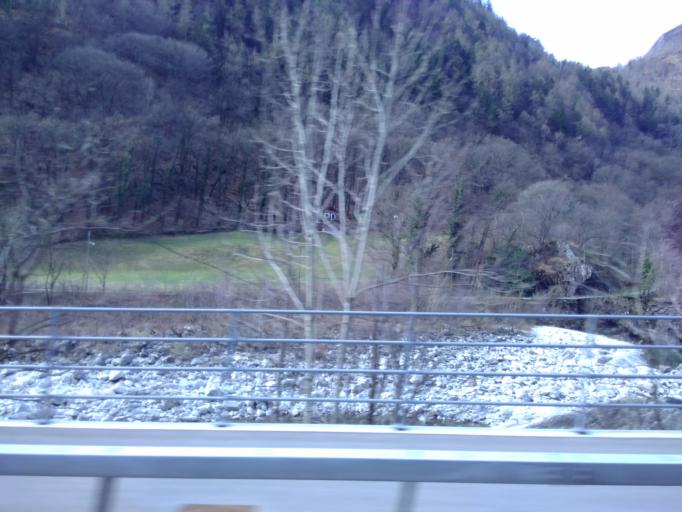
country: CH
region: Ticino
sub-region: Locarno District
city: Losone
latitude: 46.1926
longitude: 8.7559
